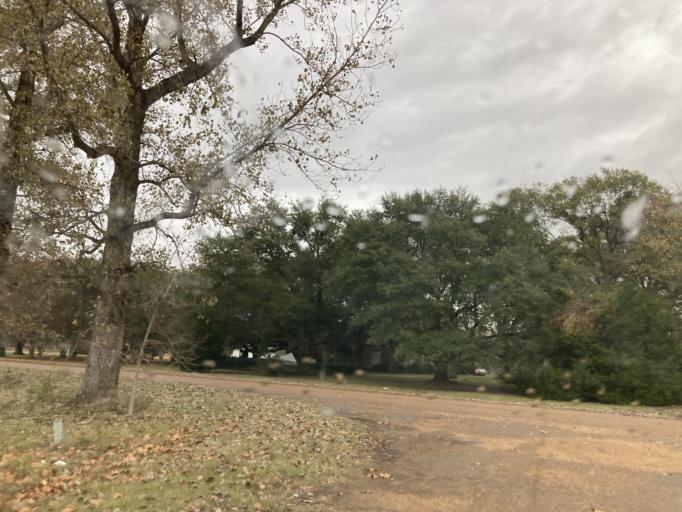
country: US
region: Mississippi
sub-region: Yazoo County
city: Yazoo City
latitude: 32.9893
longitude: -90.4481
